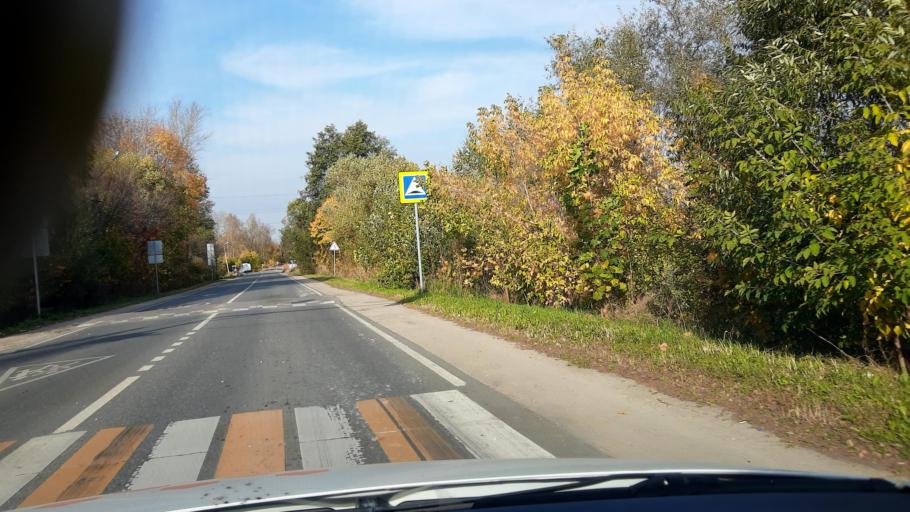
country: RU
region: Moskovskaya
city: Fryazevo
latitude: 55.7255
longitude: 38.4652
